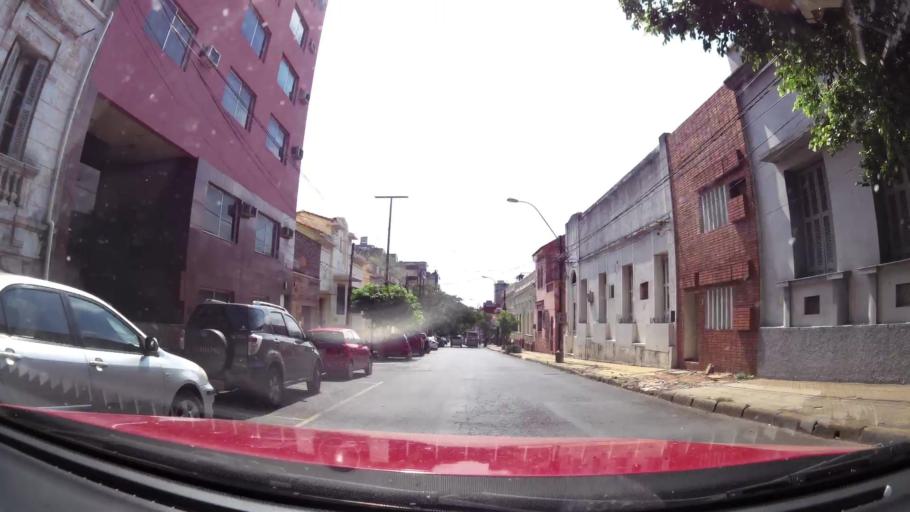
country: PY
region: Asuncion
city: Asuncion
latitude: -25.2878
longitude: -57.6249
